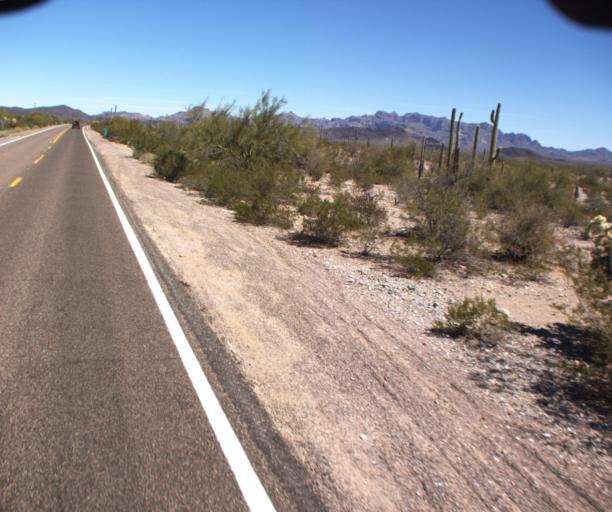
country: MX
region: Sonora
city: Sonoyta
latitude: 31.9279
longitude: -112.8019
